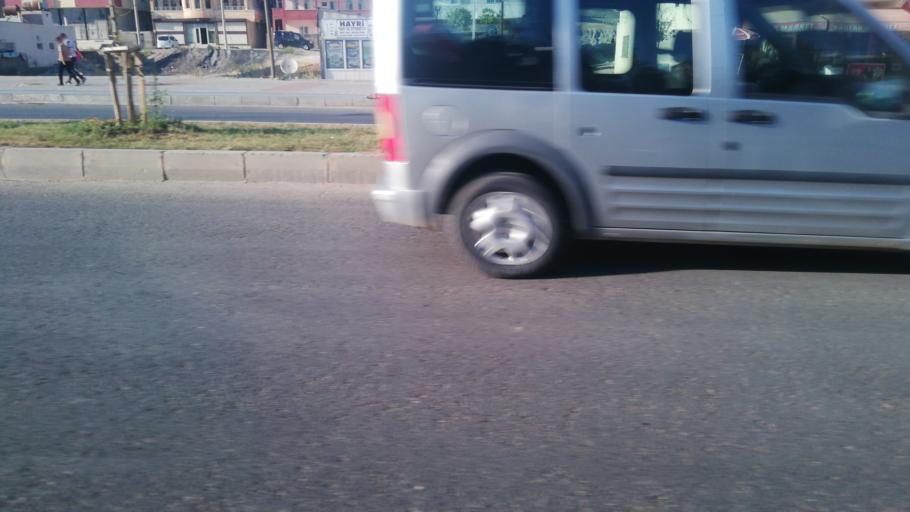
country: TR
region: Mardin
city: Midyat
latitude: 37.4179
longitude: 41.3578
